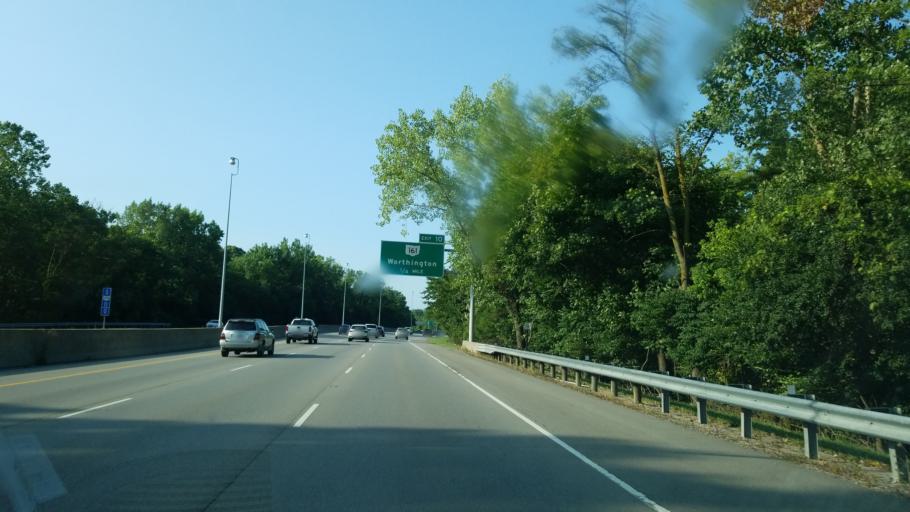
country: US
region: Ohio
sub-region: Franklin County
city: Worthington
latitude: 40.0977
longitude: -83.0369
